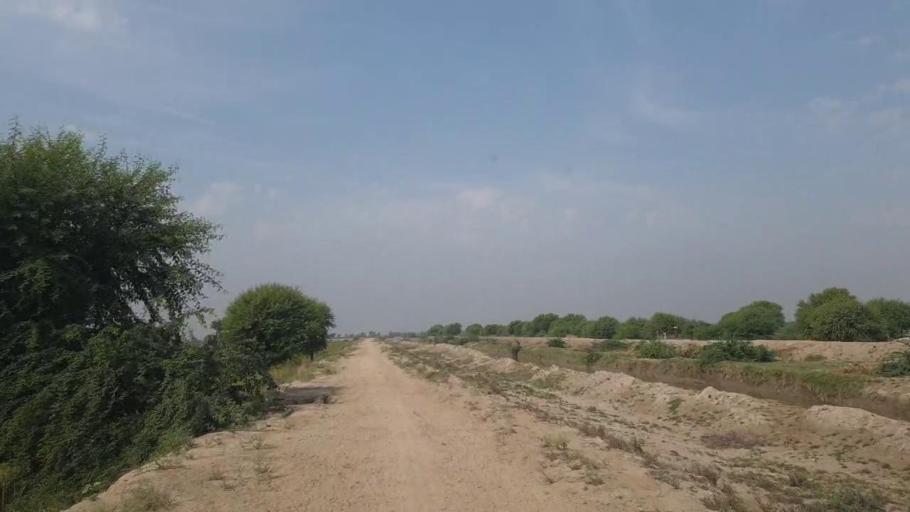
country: PK
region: Sindh
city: Tando Bago
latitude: 24.9554
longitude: 69.0299
